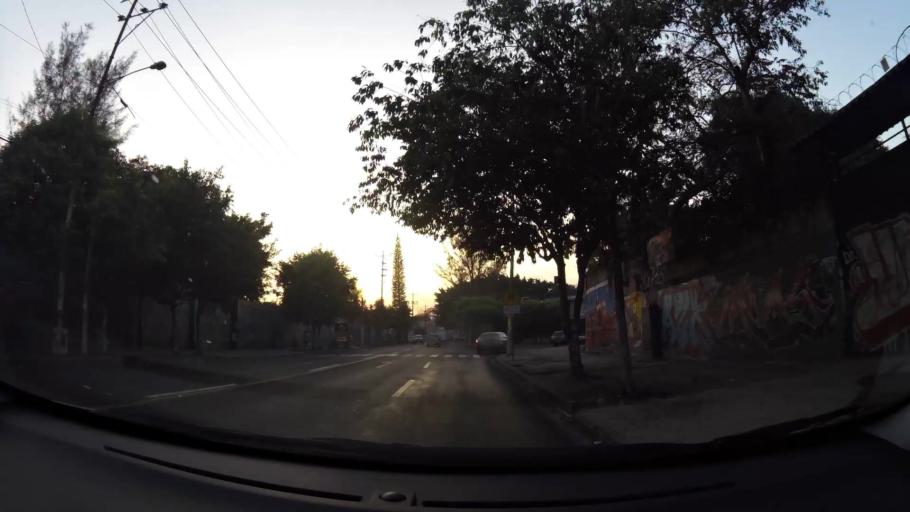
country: SV
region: San Salvador
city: Mejicanos
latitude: 13.7149
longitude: -89.2057
